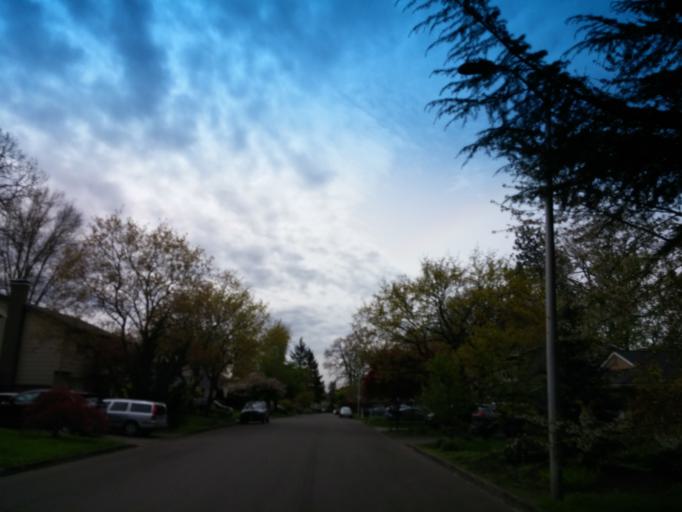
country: US
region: Oregon
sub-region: Washington County
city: Cedar Mill
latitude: 45.5330
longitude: -122.8167
